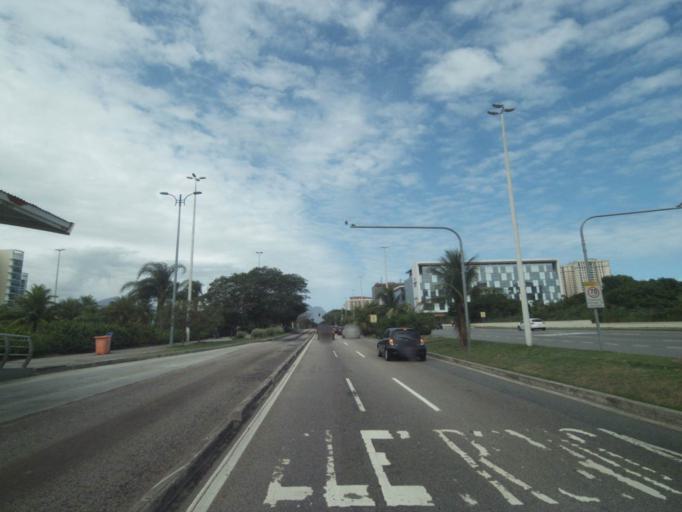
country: BR
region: Rio de Janeiro
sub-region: Nilopolis
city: Nilopolis
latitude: -23.0006
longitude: -43.3983
